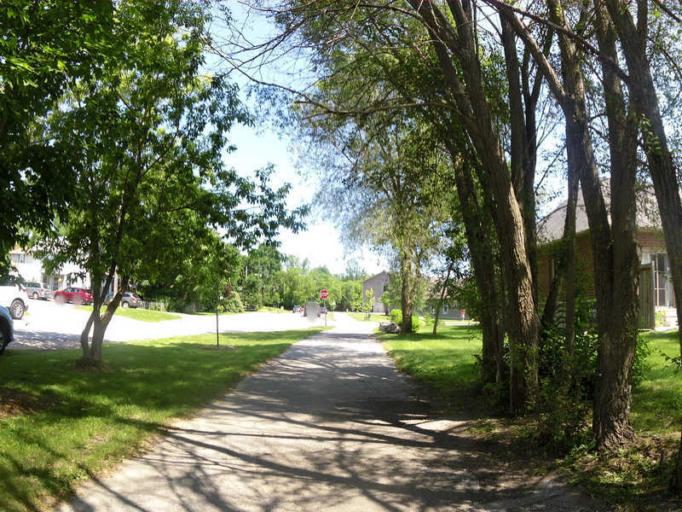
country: CA
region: Ontario
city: Peterborough
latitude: 44.4239
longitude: -78.2693
